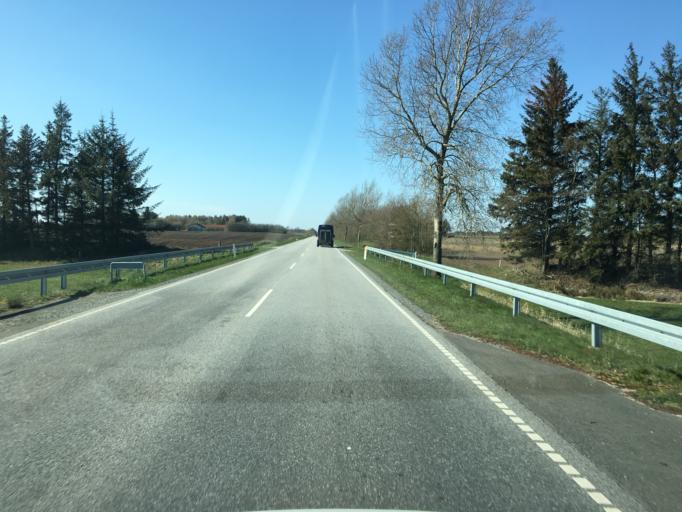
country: DK
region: South Denmark
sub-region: Aabenraa Kommune
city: Tinglev
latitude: 54.9515
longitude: 9.3439
